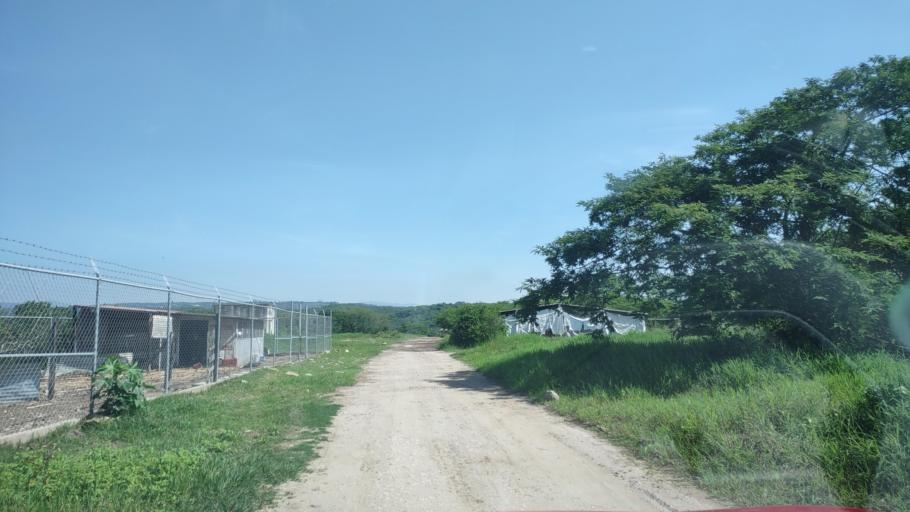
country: MX
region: Veracruz
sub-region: Emiliano Zapata
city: Dos Rios
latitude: 19.4333
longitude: -96.8038
